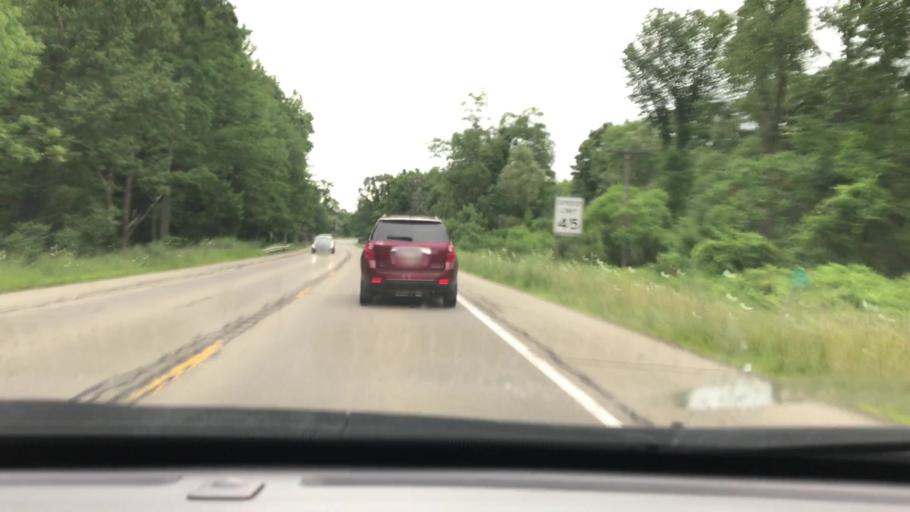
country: US
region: New York
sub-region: Erie County
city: Springville
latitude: 42.4139
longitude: -78.6911
